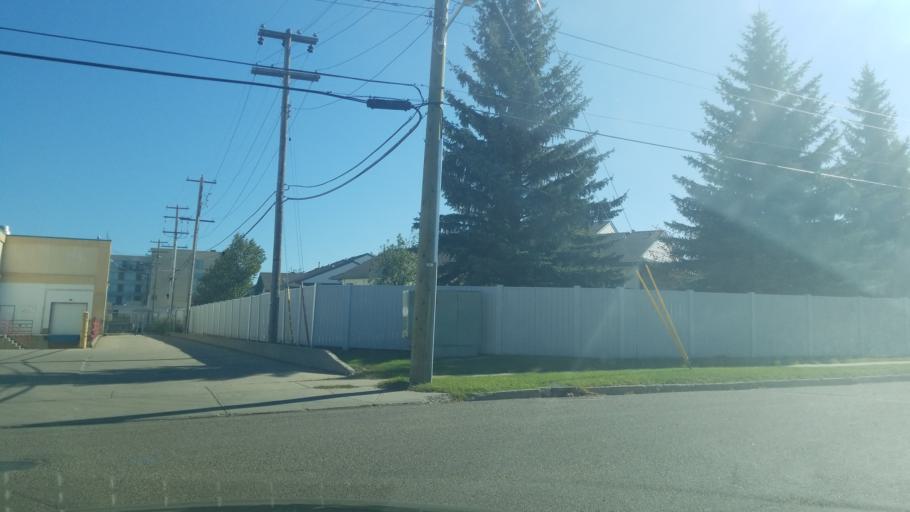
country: CA
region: Saskatchewan
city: Lloydminster
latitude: 53.2769
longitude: -110.0198
